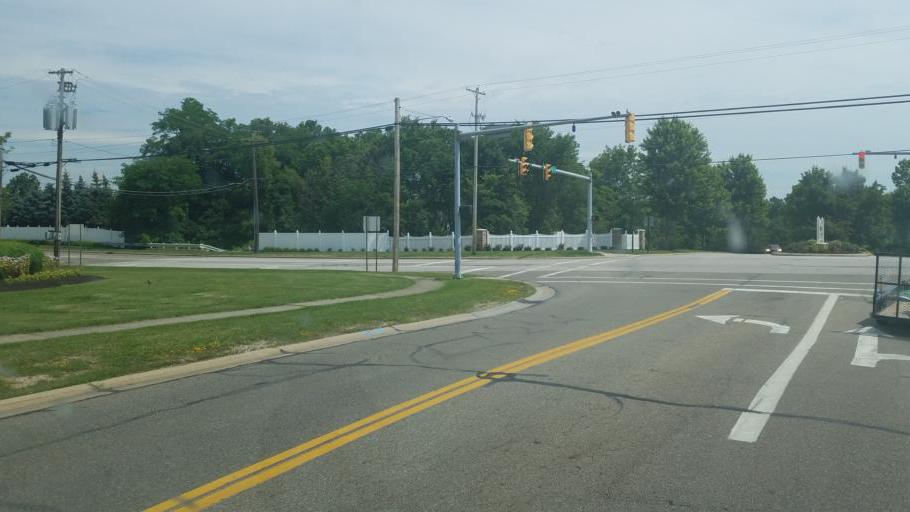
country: US
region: Ohio
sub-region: Cuyahoga County
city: Oakwood
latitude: 41.3408
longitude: -81.4788
